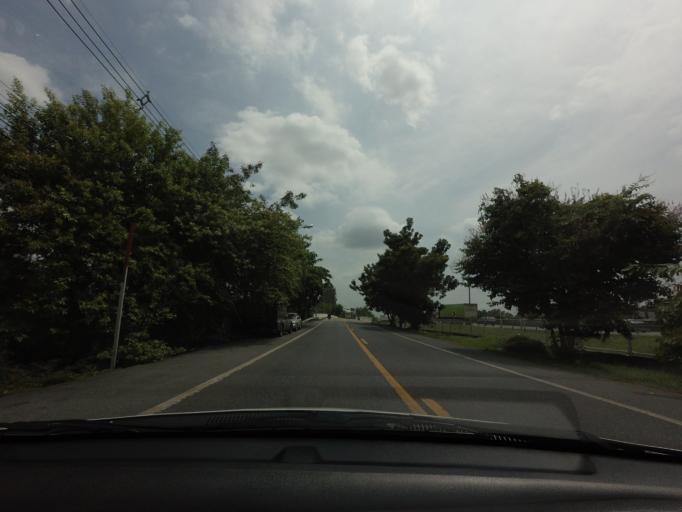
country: TH
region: Bangkok
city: Khan Na Yao
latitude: 13.8580
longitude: 100.6761
